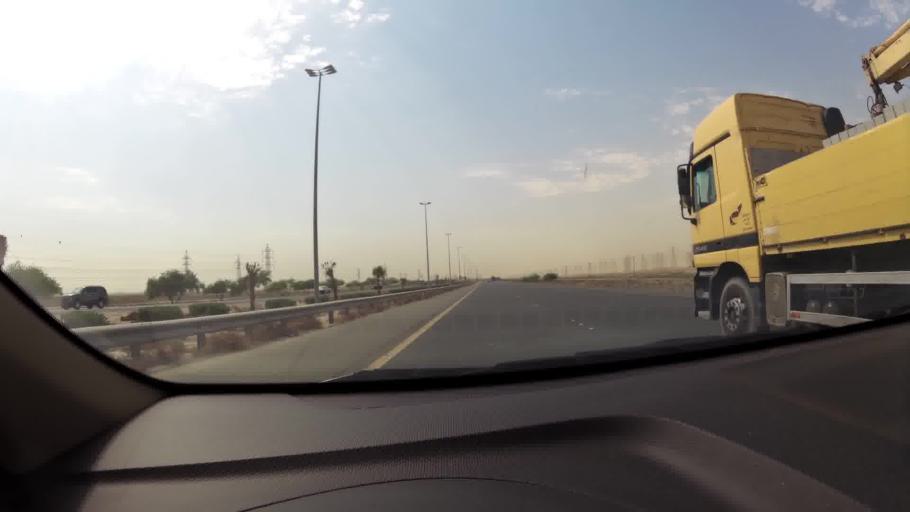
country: KW
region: Al Ahmadi
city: Al Fahahil
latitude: 28.8607
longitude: 48.2393
